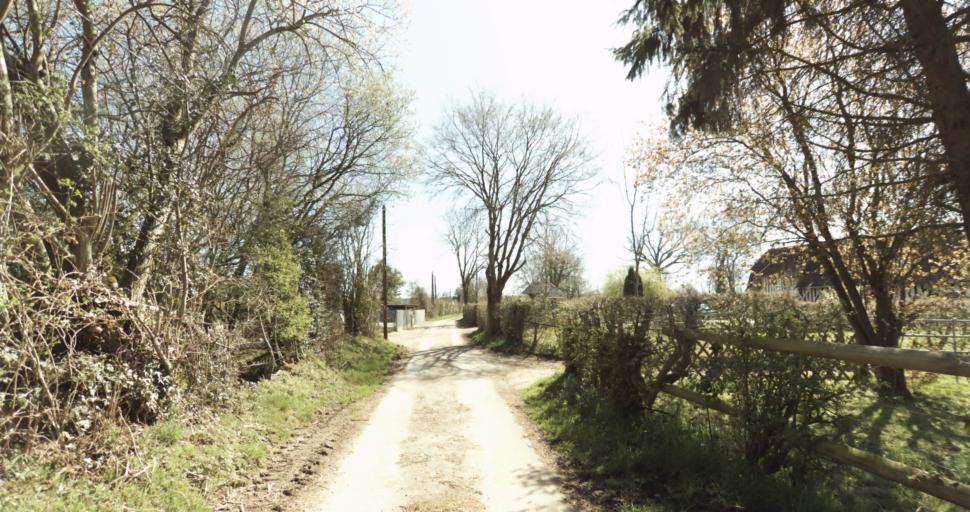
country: FR
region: Lower Normandy
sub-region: Departement du Calvados
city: Saint-Pierre-sur-Dives
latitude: 48.9950
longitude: 0.0549
